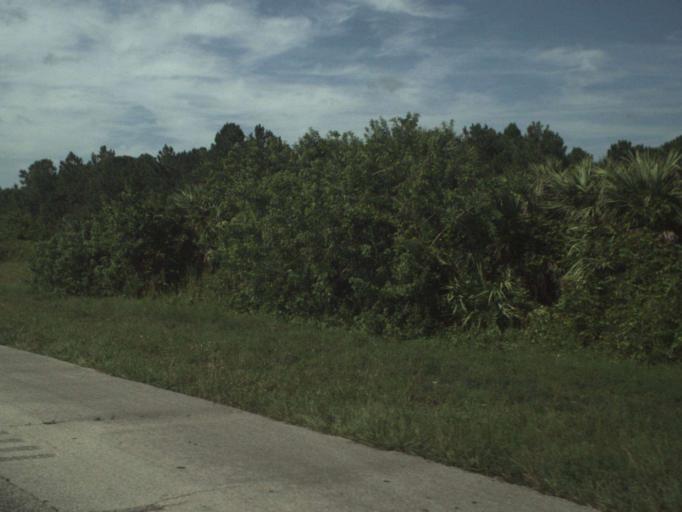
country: US
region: Florida
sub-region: Indian River County
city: Fellsmere
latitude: 27.7252
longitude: -80.5460
